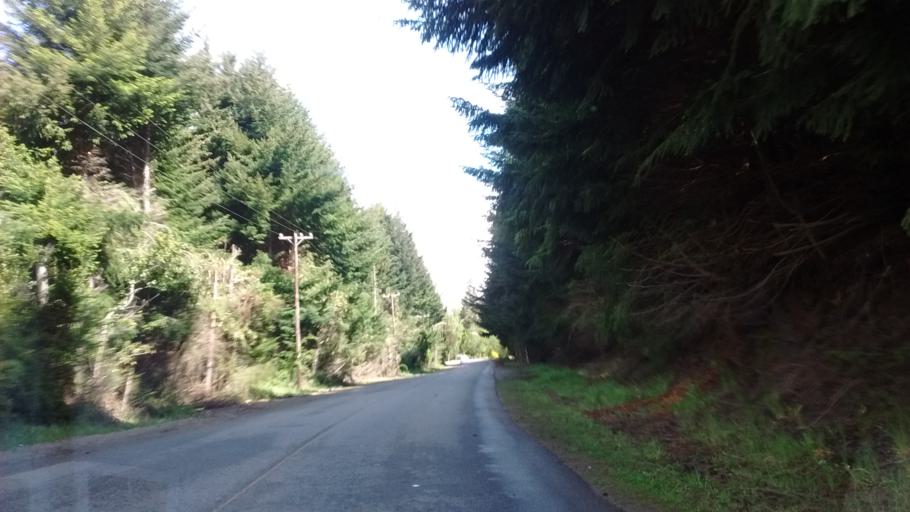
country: AR
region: Rio Negro
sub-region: Departamento de Bariloche
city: San Carlos de Bariloche
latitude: -41.0731
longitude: -71.5370
